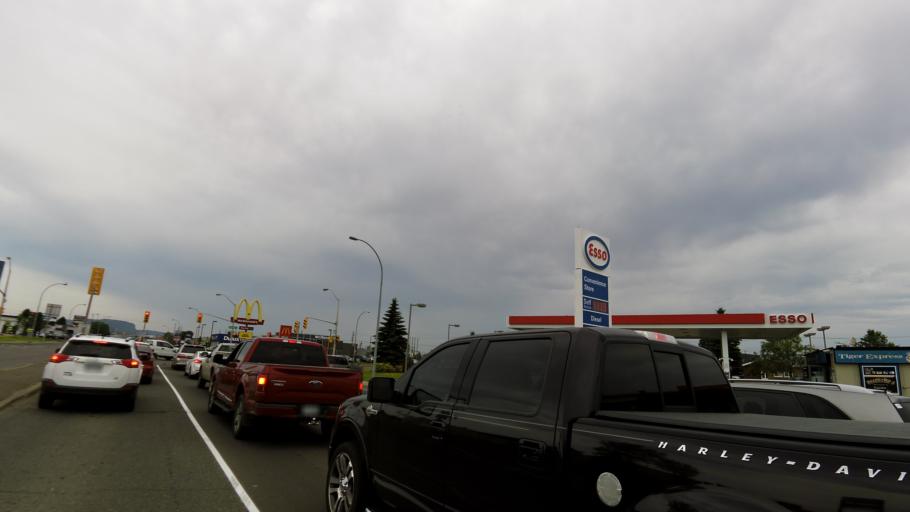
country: CA
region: Ontario
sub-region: Thunder Bay District
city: Thunder Bay
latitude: 48.4139
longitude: -89.2435
